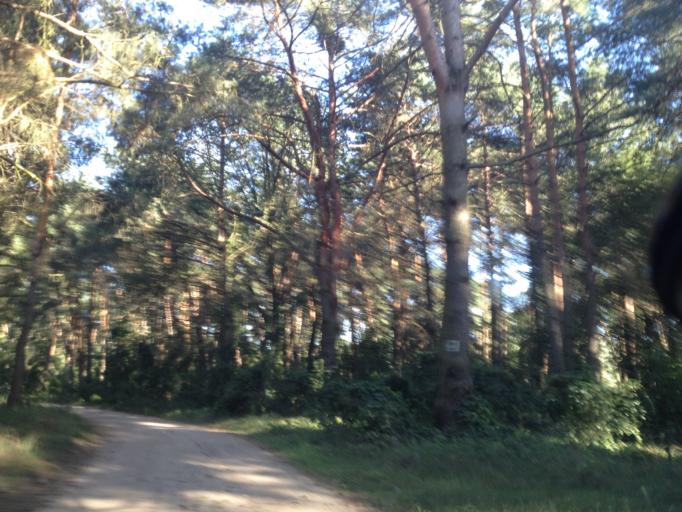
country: PL
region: Greater Poland Voivodeship
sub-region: Powiat sredzki
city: Zaniemysl
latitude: 52.1030
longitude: 17.1329
